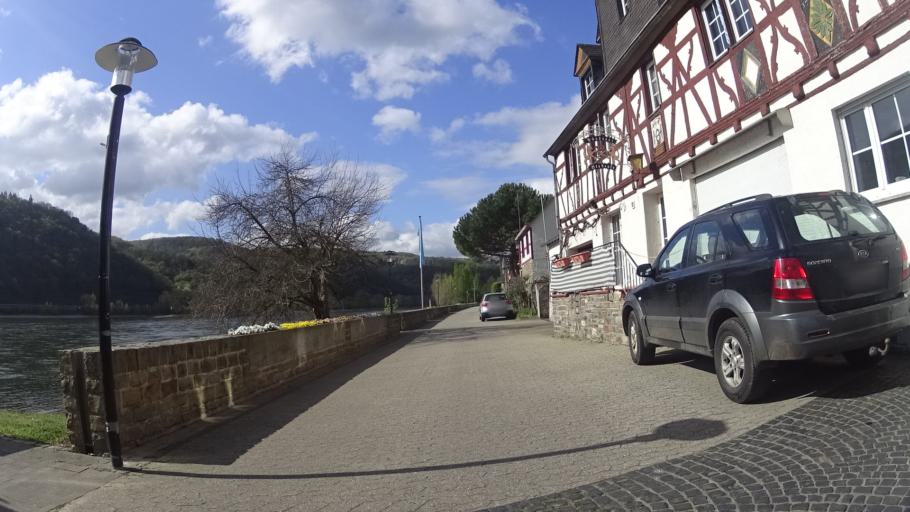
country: DE
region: Rheinland-Pfalz
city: Spay
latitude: 50.2523
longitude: 7.6477
